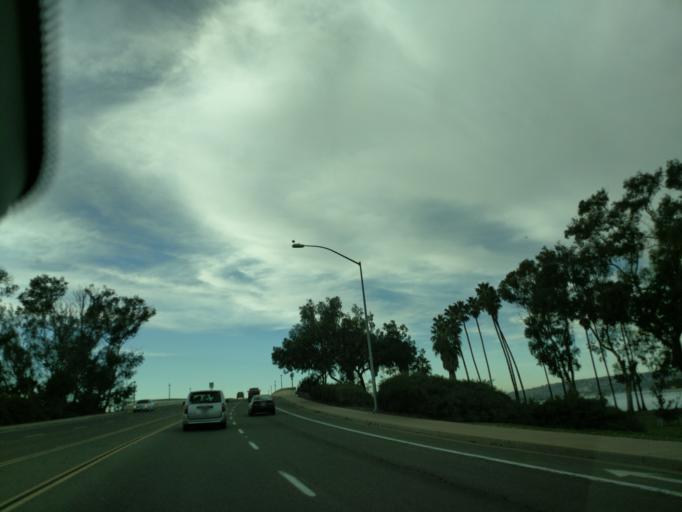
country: US
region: California
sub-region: San Diego County
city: La Jolla
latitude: 32.7663
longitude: -117.2399
